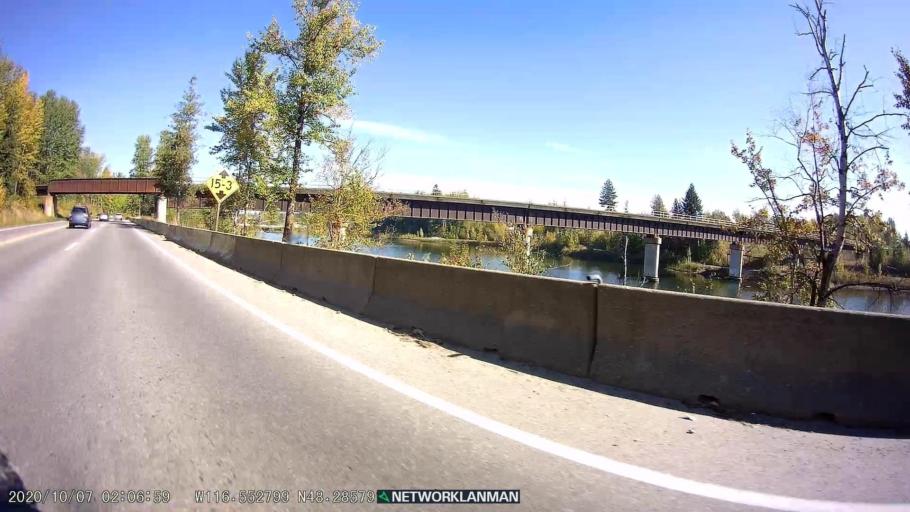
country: US
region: Idaho
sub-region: Bonner County
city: Sandpoint
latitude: 48.2864
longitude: -116.5527
